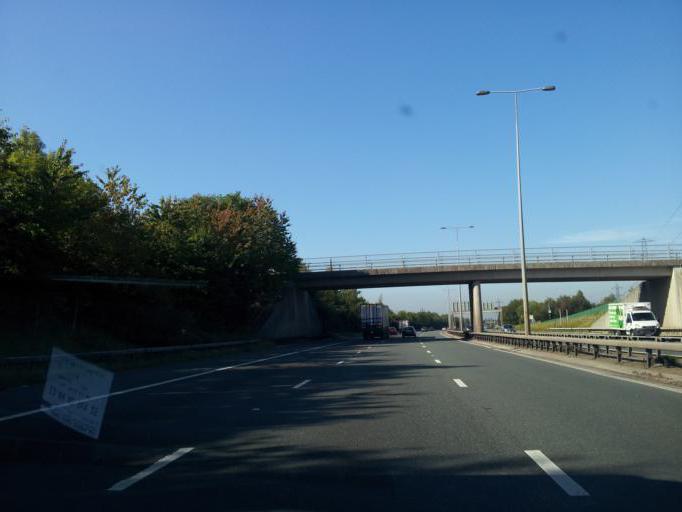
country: GB
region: England
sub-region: Borough of Rochdale
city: Middleton
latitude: 53.5283
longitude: -2.1833
